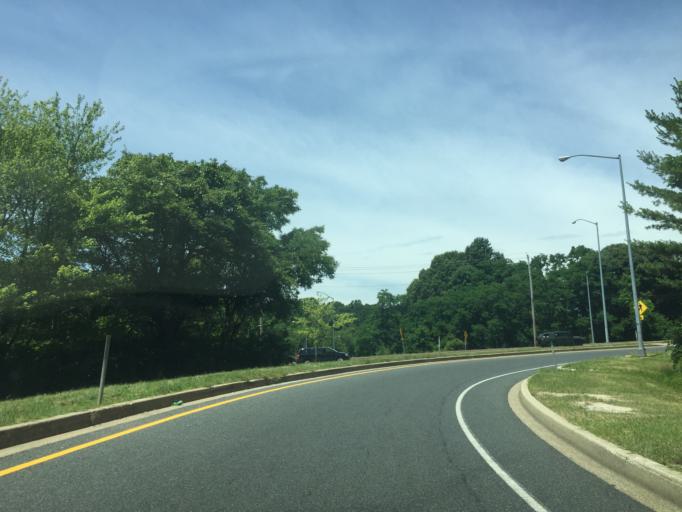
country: US
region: Maryland
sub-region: Baltimore County
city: Overlea
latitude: 39.3684
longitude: -76.5142
